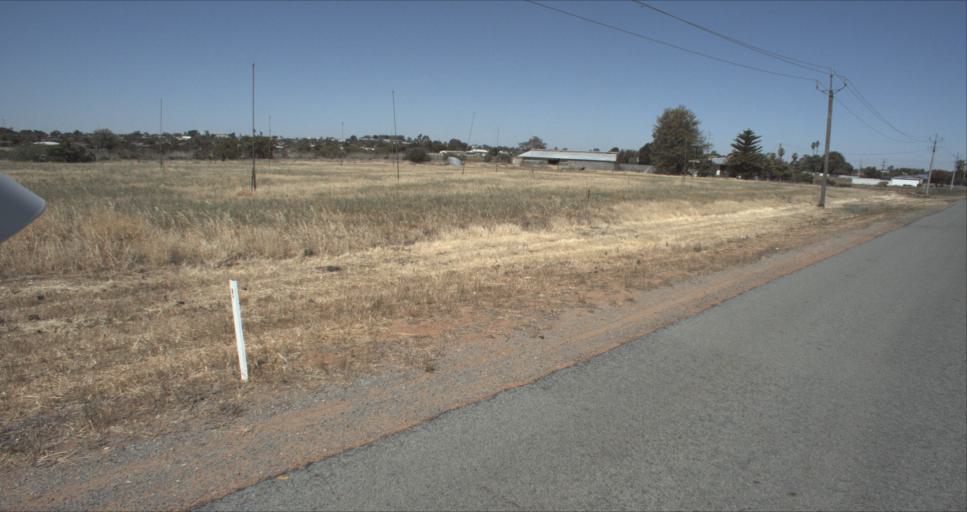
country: AU
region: New South Wales
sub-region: Leeton
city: Leeton
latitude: -34.5404
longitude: 146.3955
